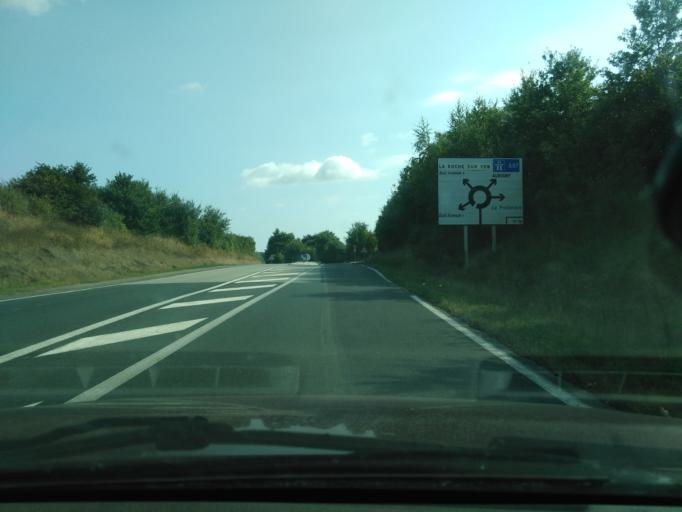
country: FR
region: Pays de la Loire
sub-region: Departement de la Vendee
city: La Roche-sur-Yon
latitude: 46.6394
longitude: -1.4403
